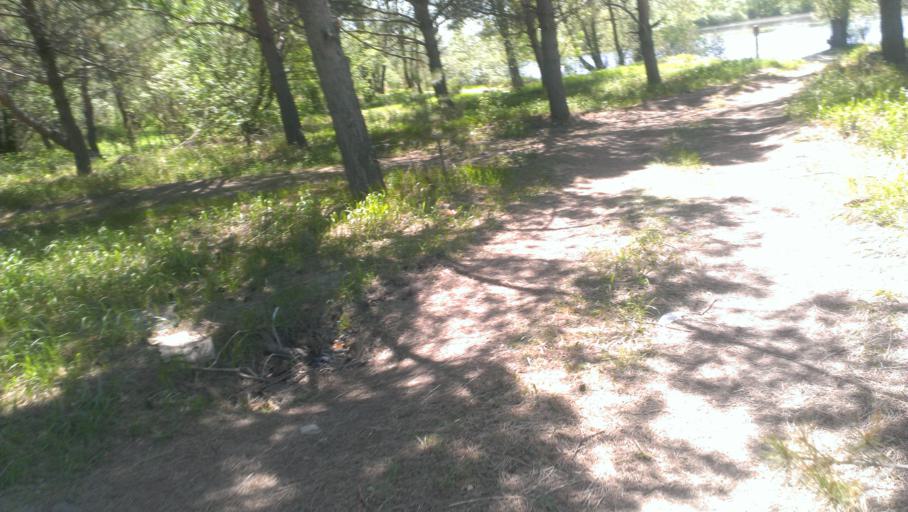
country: RU
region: Altai Krai
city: Zaton
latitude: 53.3148
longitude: 83.8510
